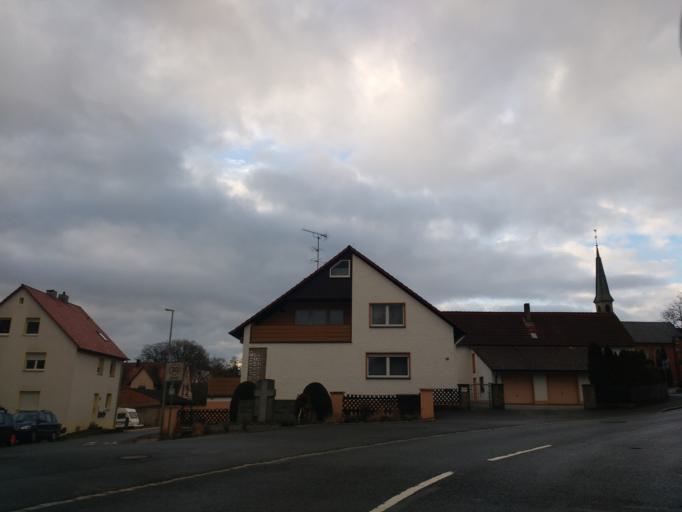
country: DE
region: Bavaria
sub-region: Regierungsbezirk Mittelfranken
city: Weisendorf
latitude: 49.5930
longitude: 10.8514
